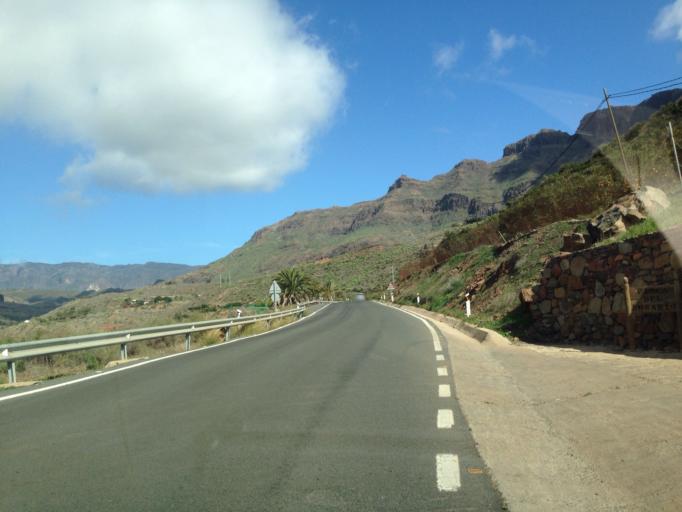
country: ES
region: Canary Islands
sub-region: Provincia de Las Palmas
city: Santa Lucia
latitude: 27.8635
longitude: -15.5665
